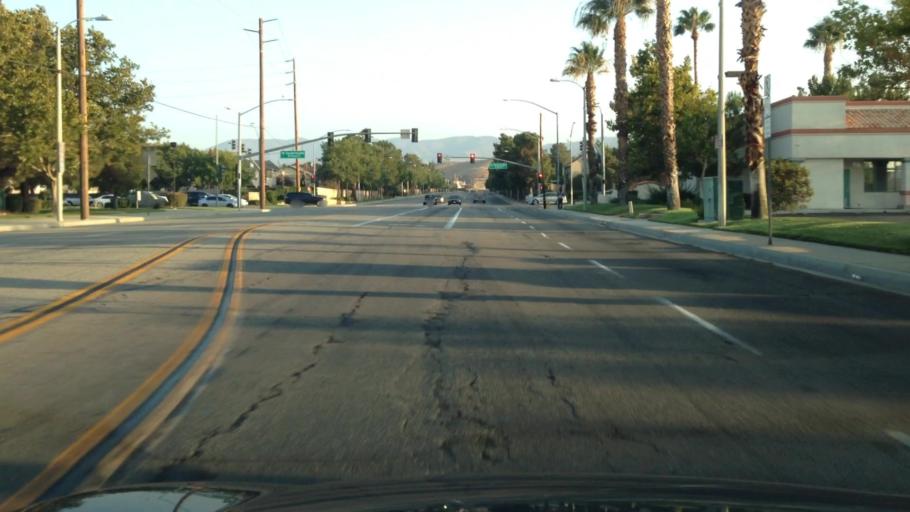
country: US
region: California
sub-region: Los Angeles County
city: Desert View Highlands
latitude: 34.6028
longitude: -118.1832
